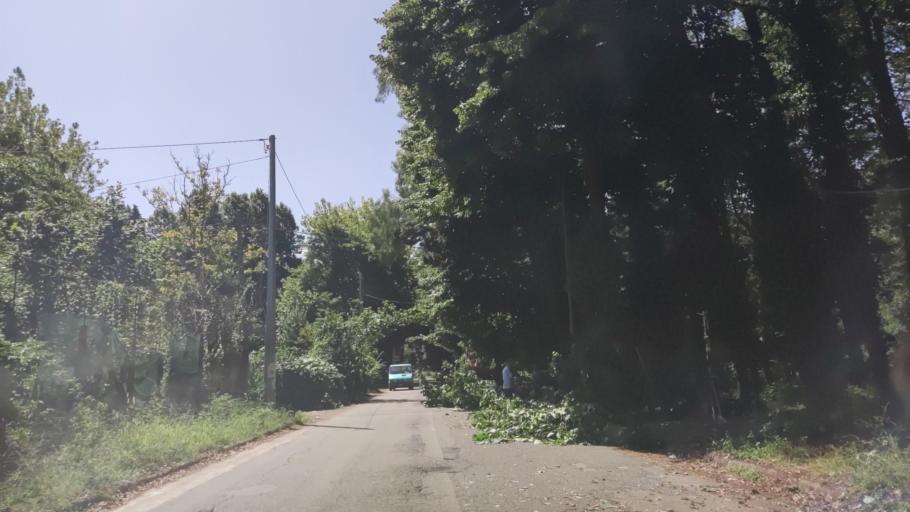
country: IT
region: Calabria
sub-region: Provincia di Reggio Calabria
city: Seminara
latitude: 38.3408
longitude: 15.8447
